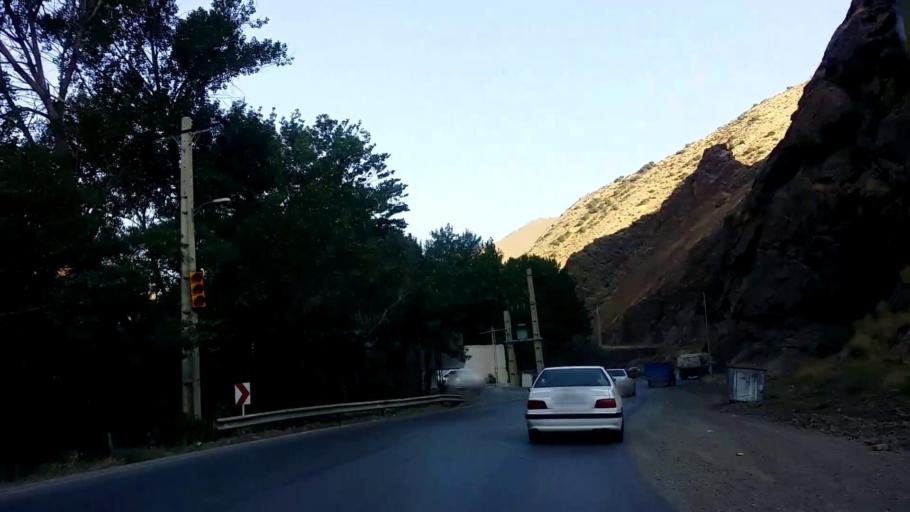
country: IR
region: Tehran
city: Tajrish
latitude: 36.0215
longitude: 51.2649
